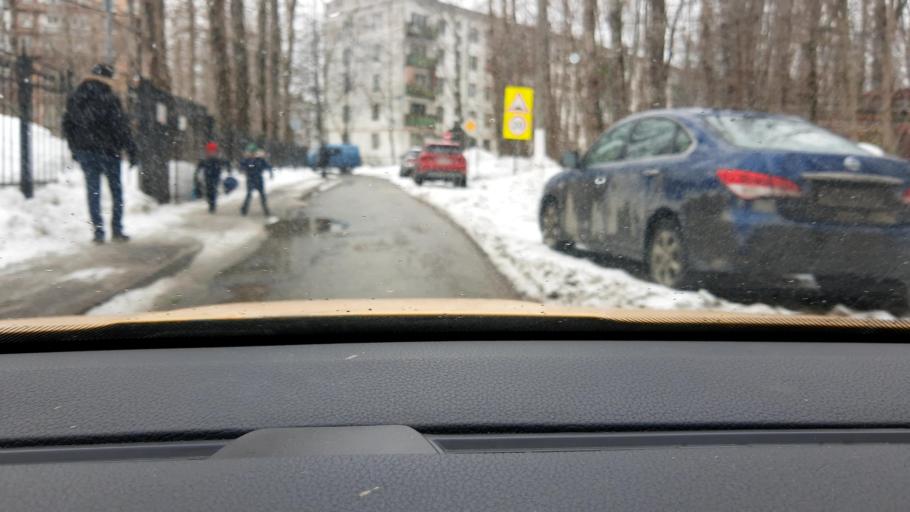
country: RU
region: Moskovskaya
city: Odintsovo
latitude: 55.6836
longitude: 37.2585
